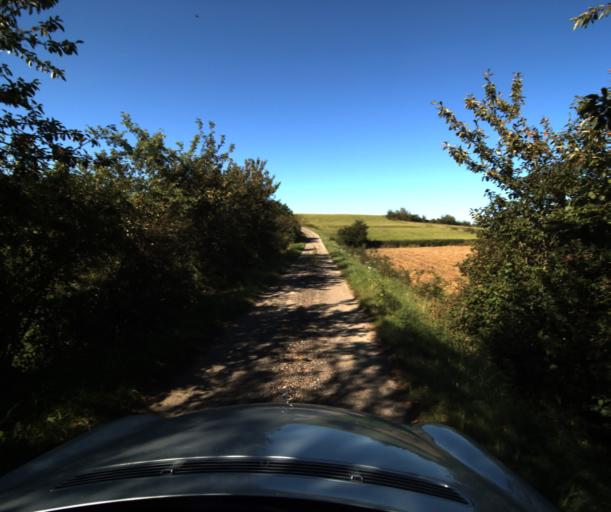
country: FR
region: Midi-Pyrenees
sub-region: Departement de l'Ariege
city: Lavelanet
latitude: 42.9706
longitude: 1.8882
